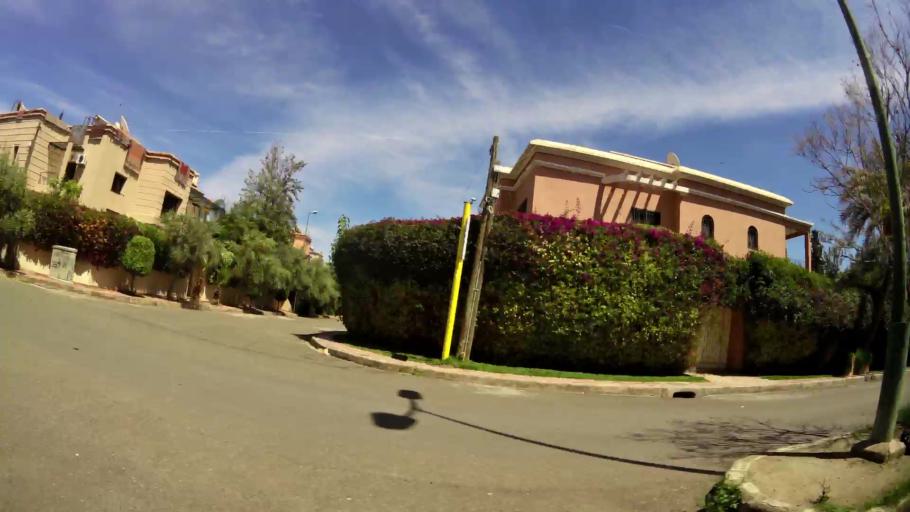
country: MA
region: Marrakech-Tensift-Al Haouz
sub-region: Marrakech
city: Marrakesh
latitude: 31.6450
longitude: -8.0622
